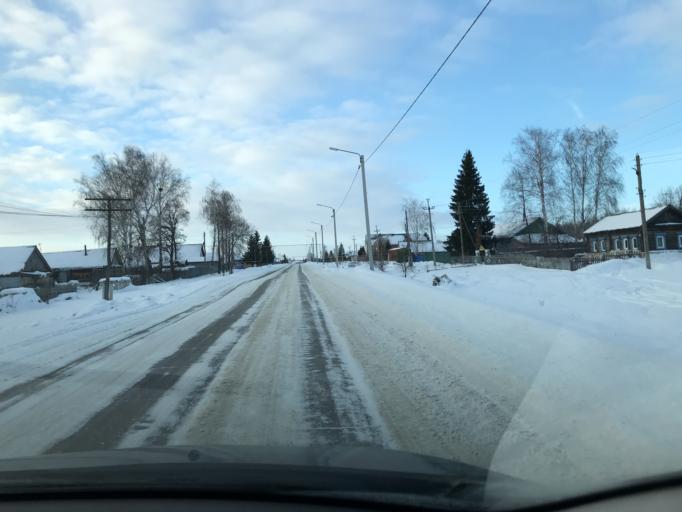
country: RU
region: Ulyanovsk
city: Undory
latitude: 54.6035
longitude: 48.4125
